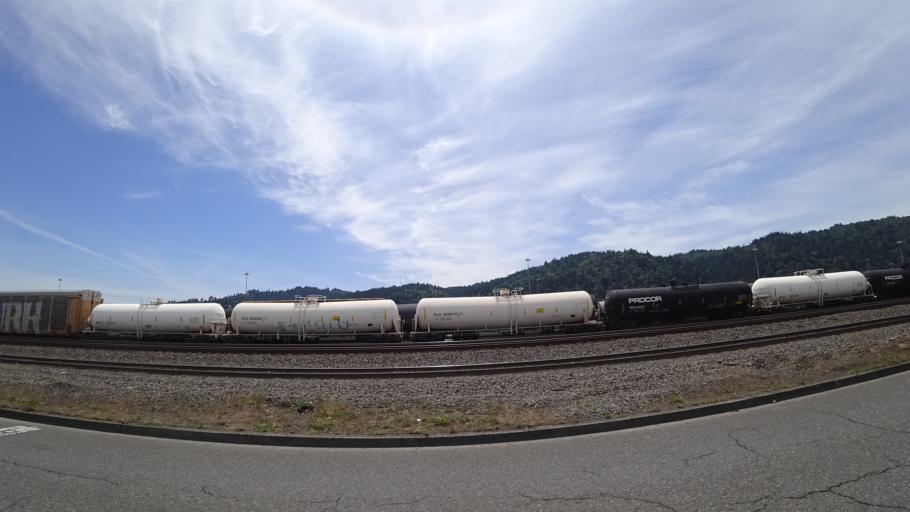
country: US
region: Oregon
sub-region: Multnomah County
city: Portland
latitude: 45.5523
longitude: -122.7160
